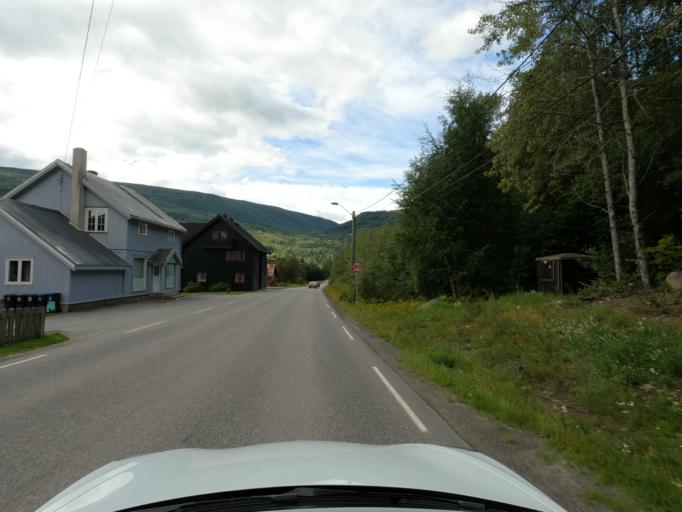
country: NO
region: Telemark
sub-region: Tinn
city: Rjukan
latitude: 59.9913
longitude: 8.7429
